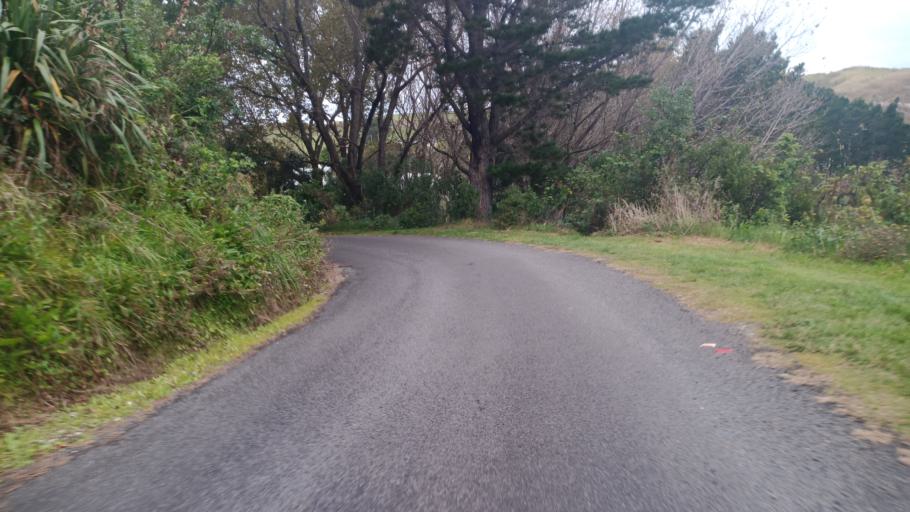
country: NZ
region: Gisborne
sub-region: Gisborne District
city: Gisborne
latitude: -38.6836
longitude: 178.0387
